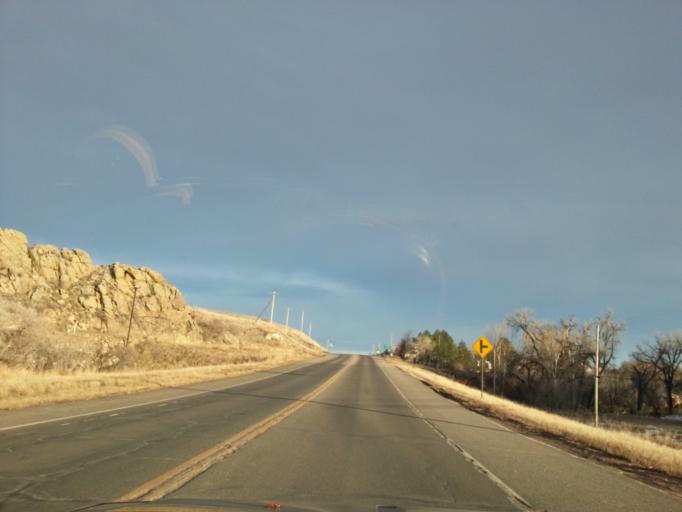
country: US
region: Colorado
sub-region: Larimer County
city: Loveland
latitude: 40.4084
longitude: -105.1541
